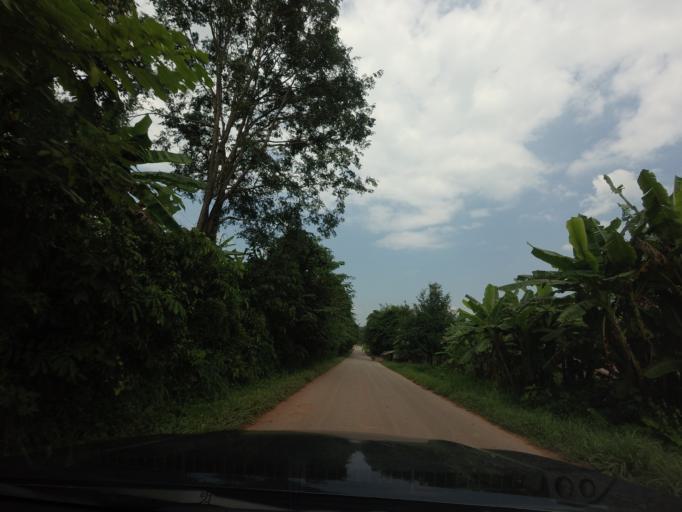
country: TH
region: Uttaradit
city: Fak Tha
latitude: 17.7979
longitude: 100.9326
